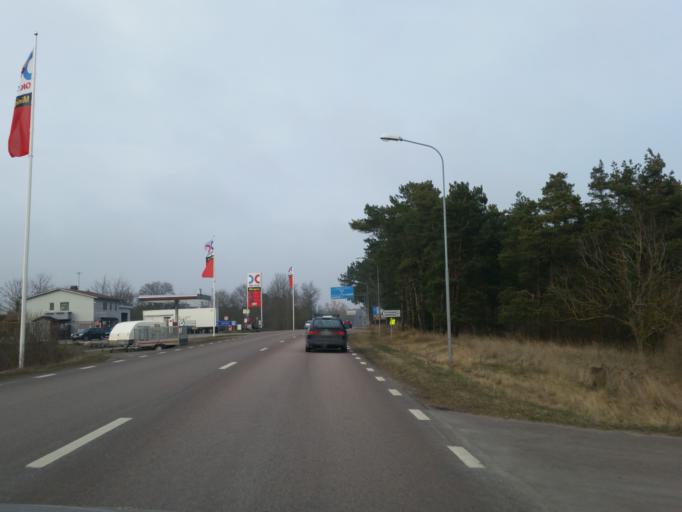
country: SE
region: Kalmar
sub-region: Borgholms Kommun
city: Borgholm
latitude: 57.1626
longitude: 17.0119
